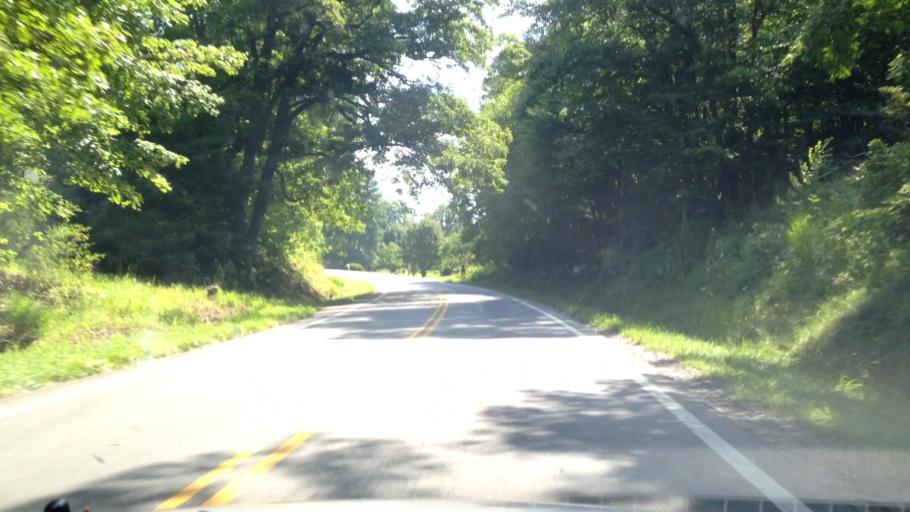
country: US
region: Virginia
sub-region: Patrick County
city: Stuart
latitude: 36.5768
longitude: -80.3748
